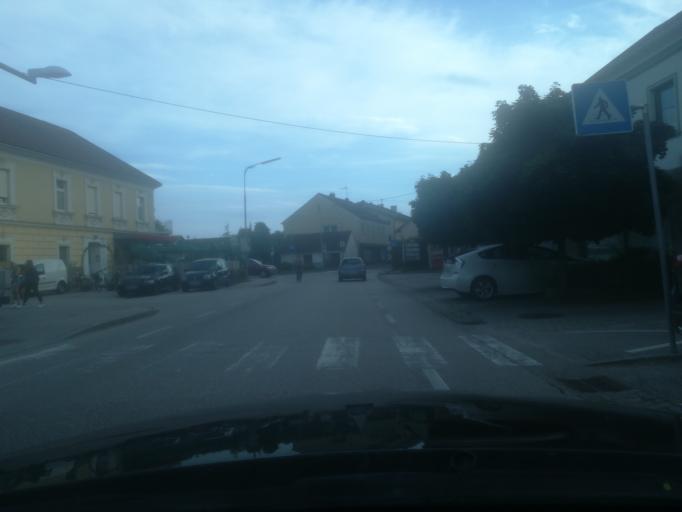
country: AT
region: Upper Austria
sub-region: Politischer Bezirk Perg
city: Perg
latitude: 48.2759
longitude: 14.5798
